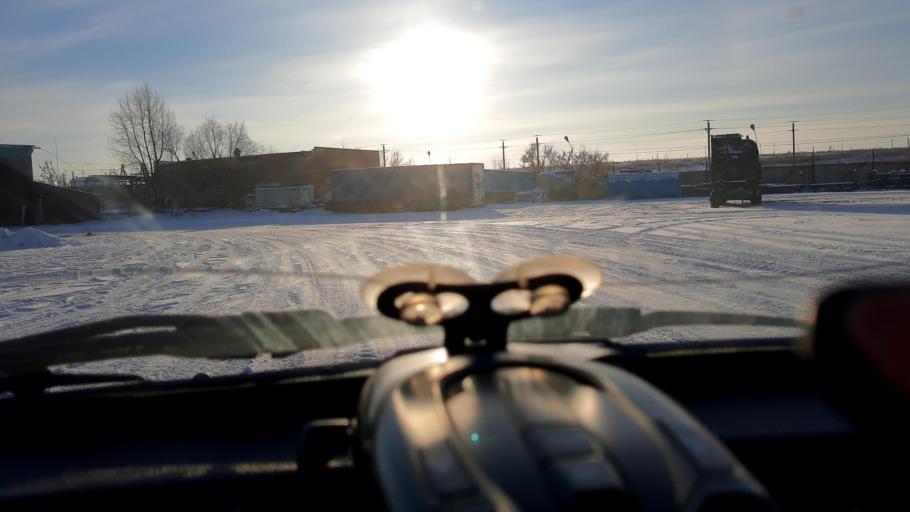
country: RU
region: Bashkortostan
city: Avdon
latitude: 54.6073
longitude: 55.8435
